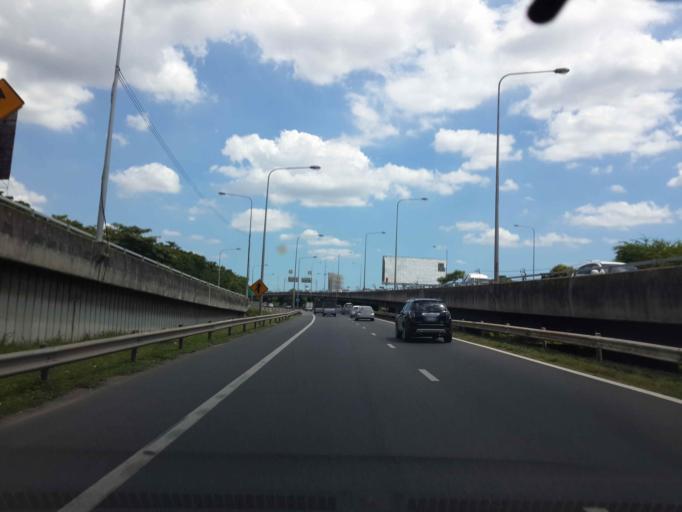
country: TH
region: Bangkok
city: Chom Thong
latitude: 13.6799
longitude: 100.4773
